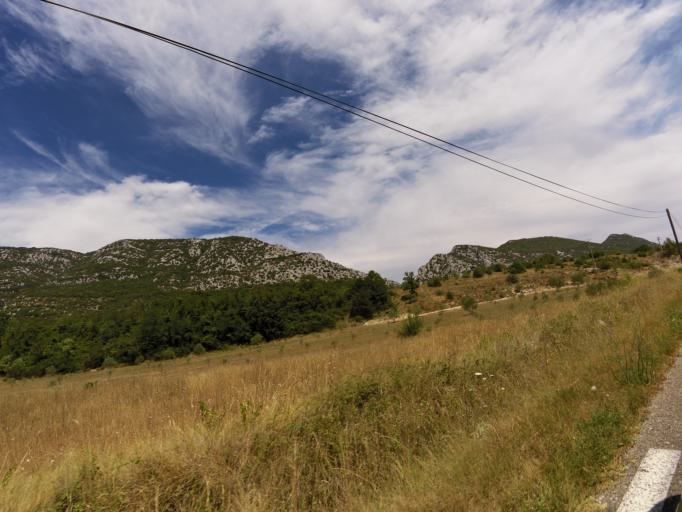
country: FR
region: Languedoc-Roussillon
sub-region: Departement du Gard
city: Saint-Hippolyte-du-Fort
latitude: 43.9525
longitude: 3.8002
